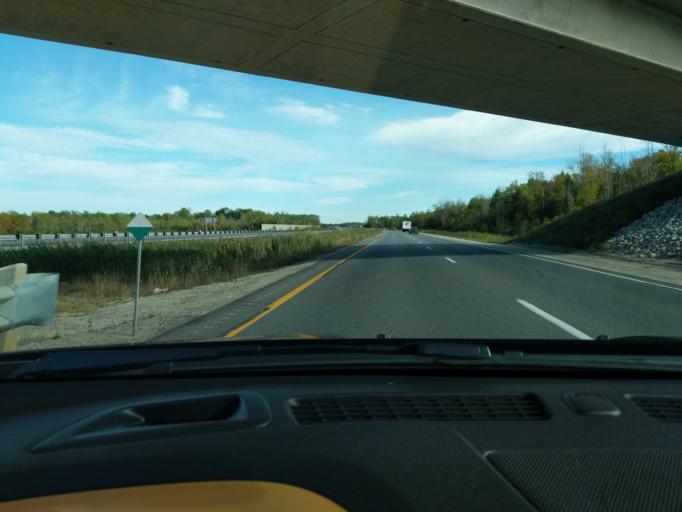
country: CA
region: Ontario
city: Collingwood
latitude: 44.4702
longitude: -80.1407
